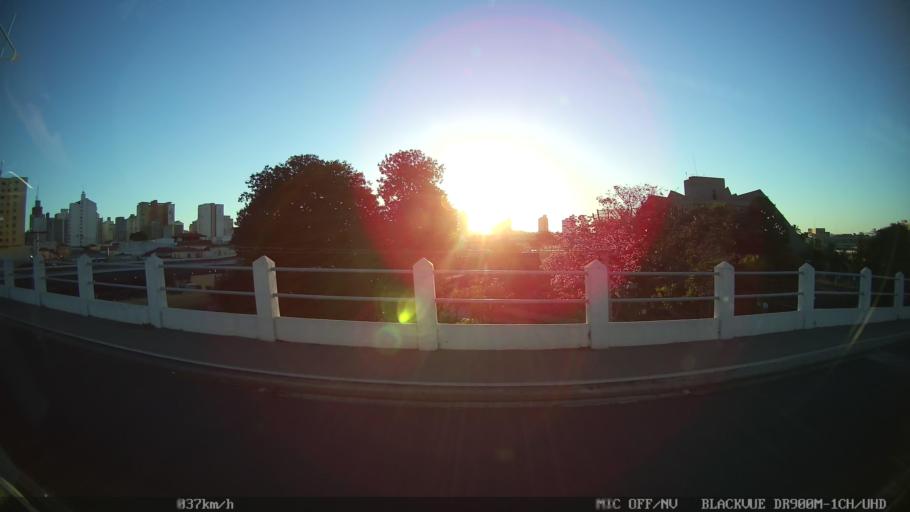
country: BR
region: Sao Paulo
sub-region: Sao Jose Do Rio Preto
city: Sao Jose do Rio Preto
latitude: -20.8096
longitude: -49.3749
